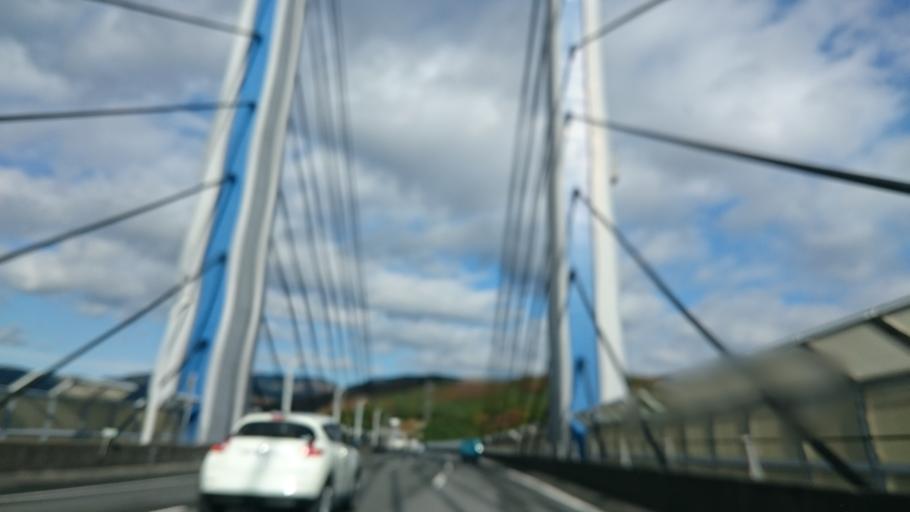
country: JP
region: Shizuoka
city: Gotemba
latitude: 35.3418
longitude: 138.9786
